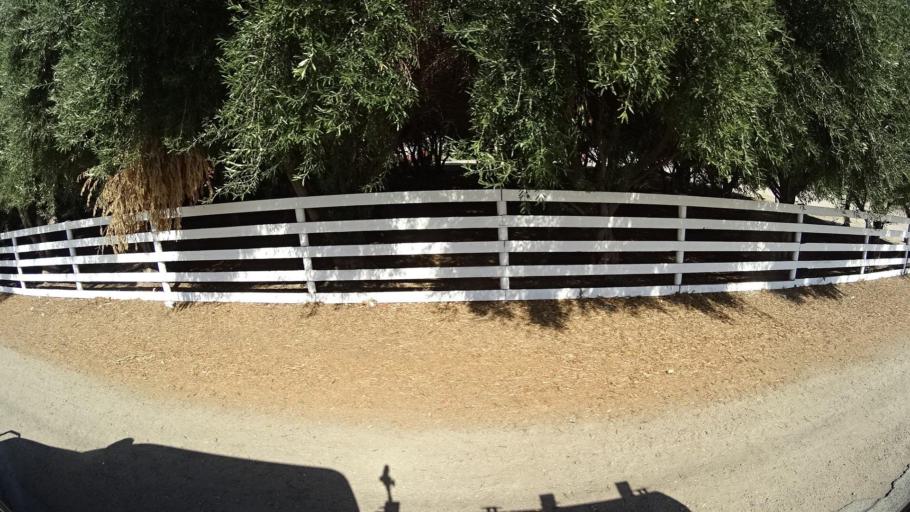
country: US
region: California
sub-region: Monterey County
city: Greenfield
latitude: 36.3075
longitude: -121.2609
